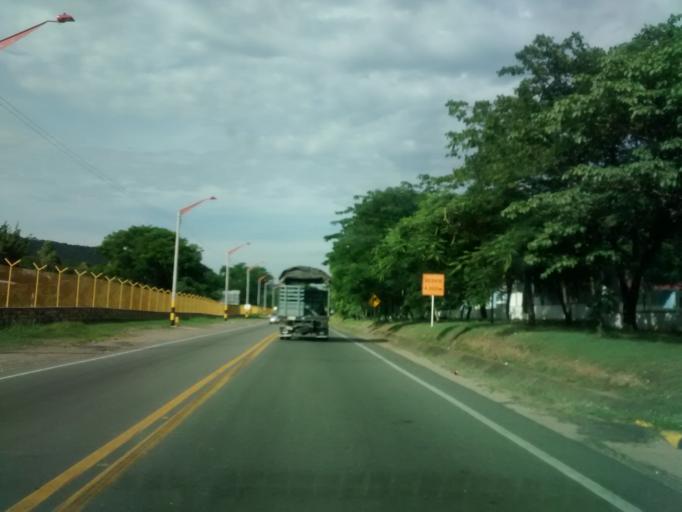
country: CO
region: Tolima
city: Melgar
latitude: 4.2206
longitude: -74.6266
